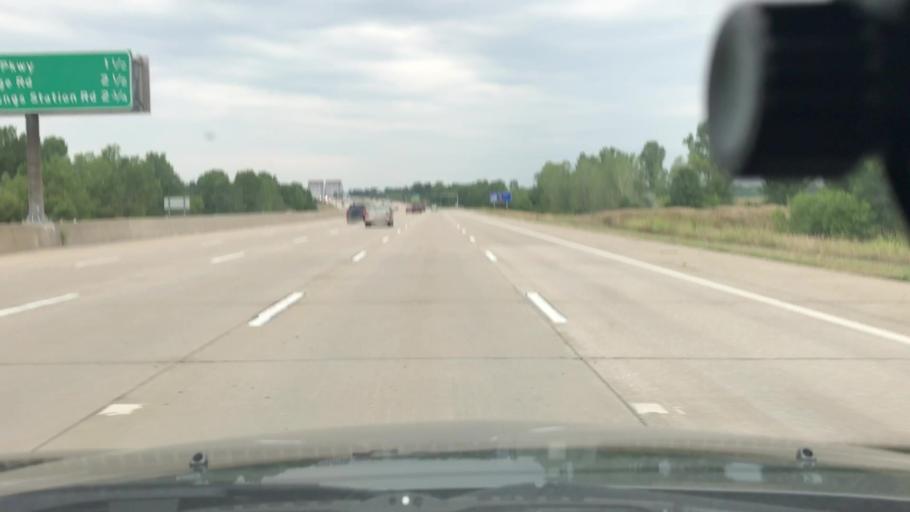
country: US
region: Missouri
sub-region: Saint Charles County
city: Saint Charles
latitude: 38.7235
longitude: -90.5126
